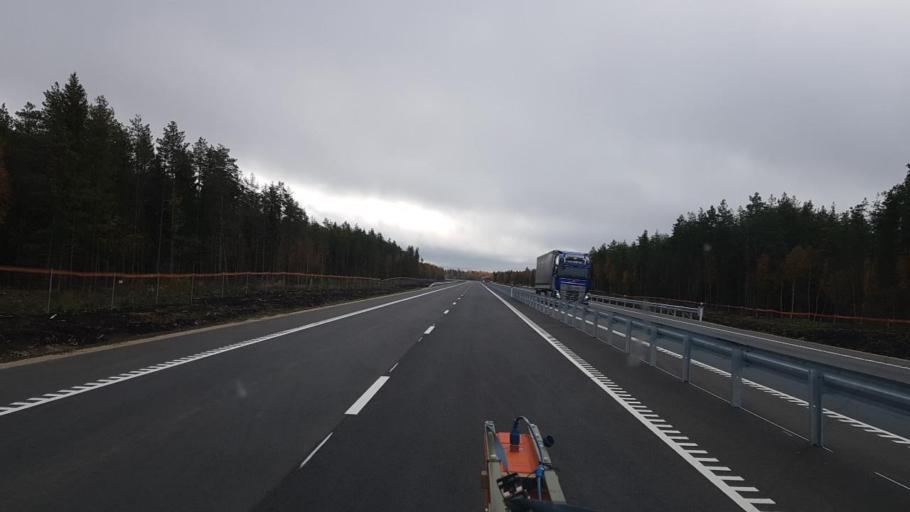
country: EE
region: Jaervamaa
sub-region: Paide linn
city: Paide
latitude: 59.0198
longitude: 25.5488
